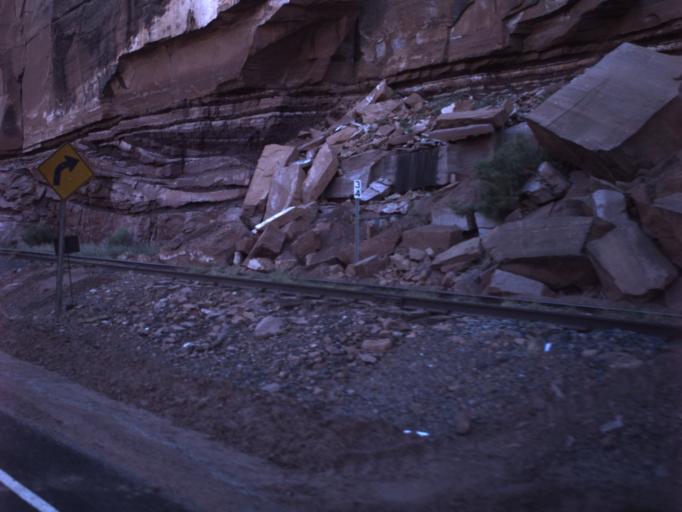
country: US
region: Utah
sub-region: Grand County
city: Moab
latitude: 38.5550
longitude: -109.6525
